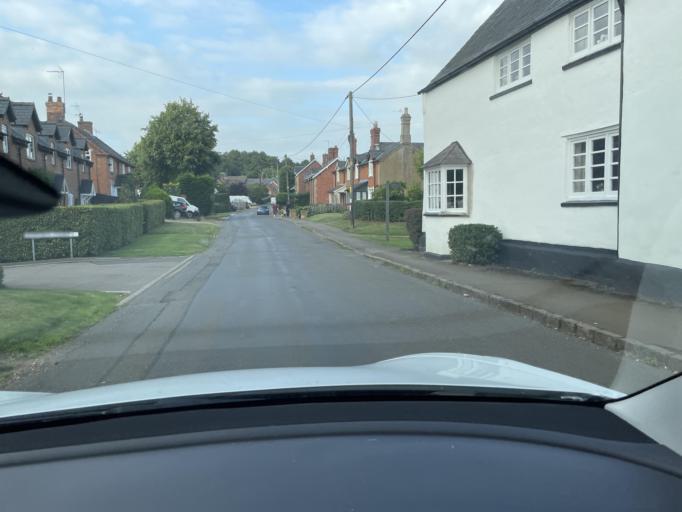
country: GB
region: England
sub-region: Northamptonshire
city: Brixworth
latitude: 52.3938
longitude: -0.9894
